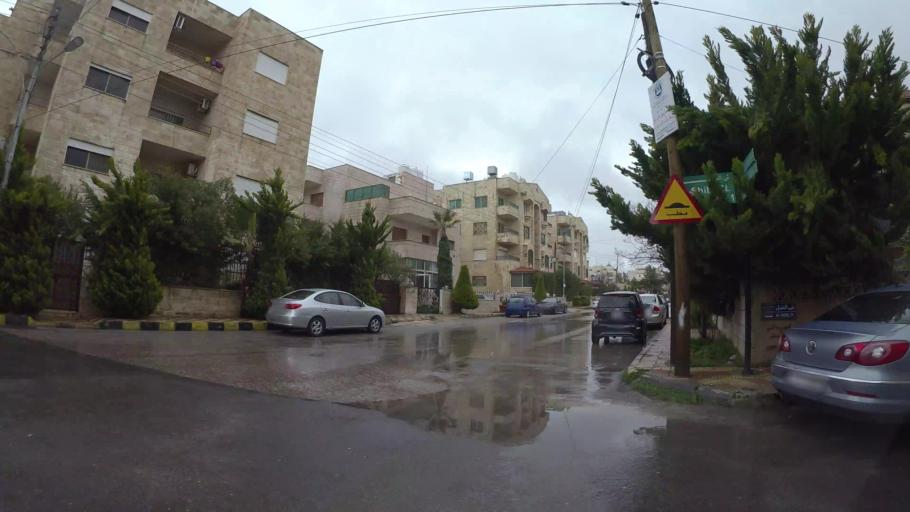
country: JO
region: Amman
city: Wadi as Sir
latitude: 31.9680
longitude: 35.8624
